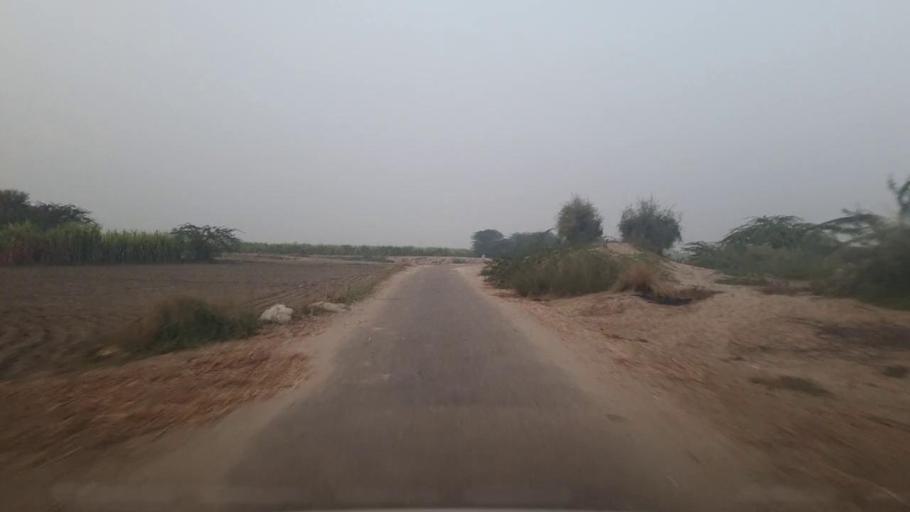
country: PK
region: Sindh
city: Kot Diji
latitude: 27.3395
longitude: 68.6167
